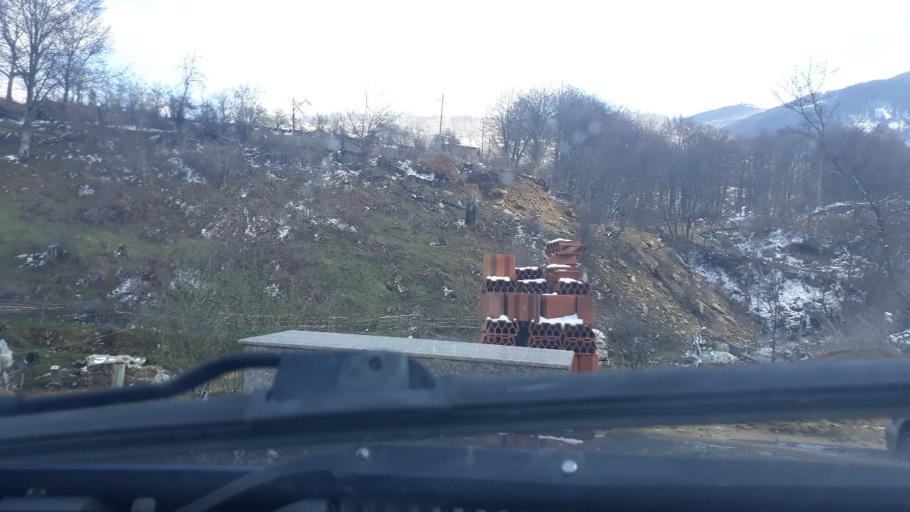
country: MK
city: Bogomila
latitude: 41.7181
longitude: 21.4832
